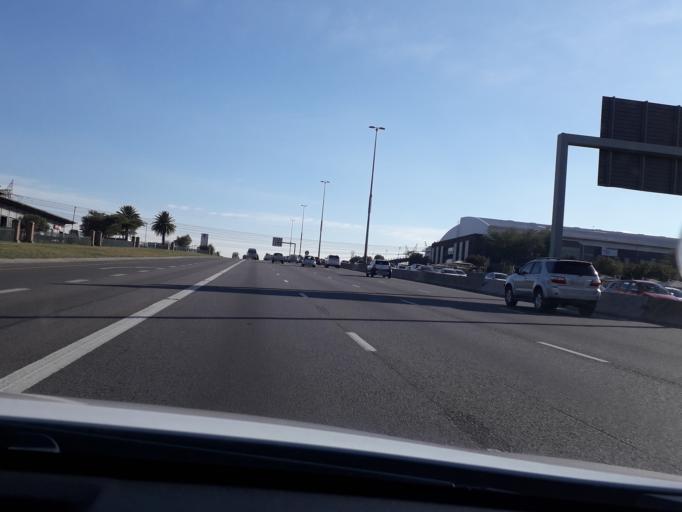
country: ZA
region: Gauteng
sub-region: City of Johannesburg Metropolitan Municipality
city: Midrand
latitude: -25.9234
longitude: 28.1482
